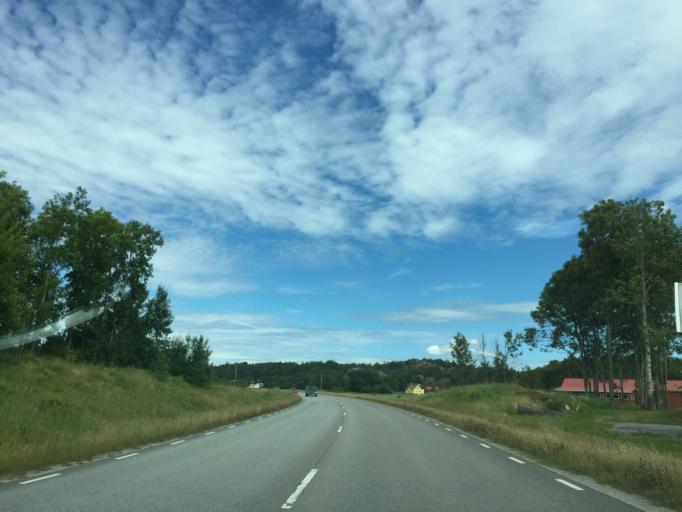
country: SE
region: Vaestra Goetaland
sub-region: Tjorns Kommun
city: Skaerhamn
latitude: 58.0023
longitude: 11.6067
